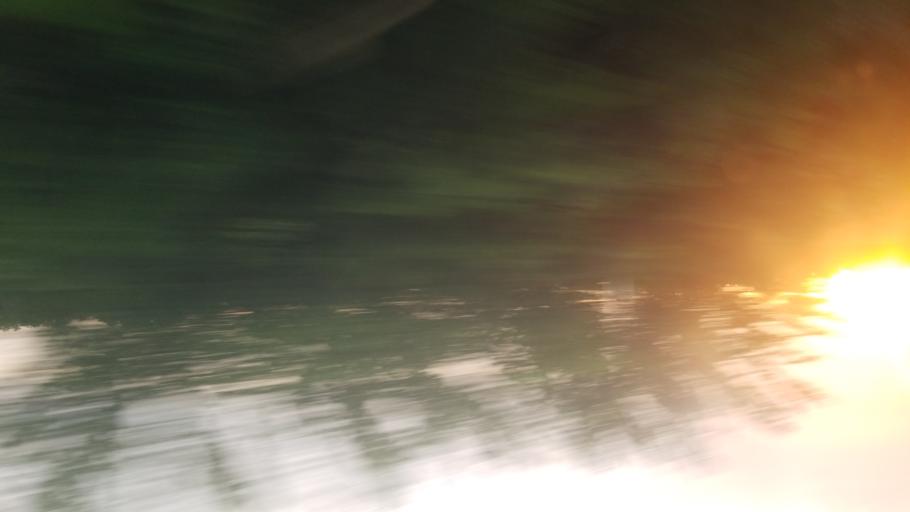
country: US
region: Kansas
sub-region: Marion County
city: Peabody
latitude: 38.1551
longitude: -97.1194
